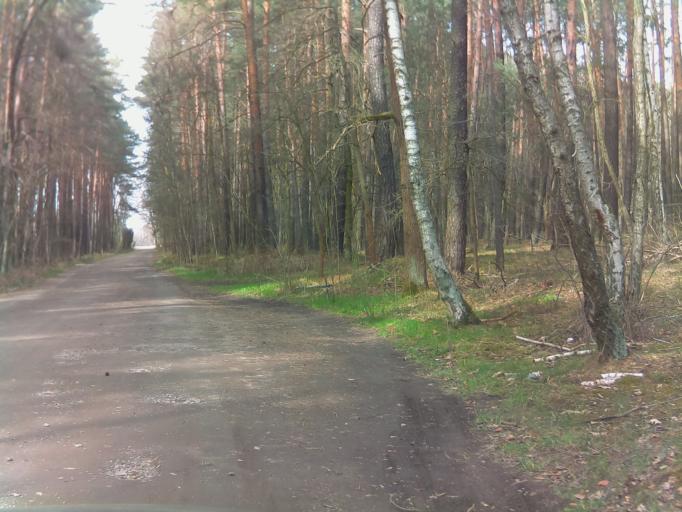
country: DE
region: Brandenburg
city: Cottbus
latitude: 51.7981
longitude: 14.3381
